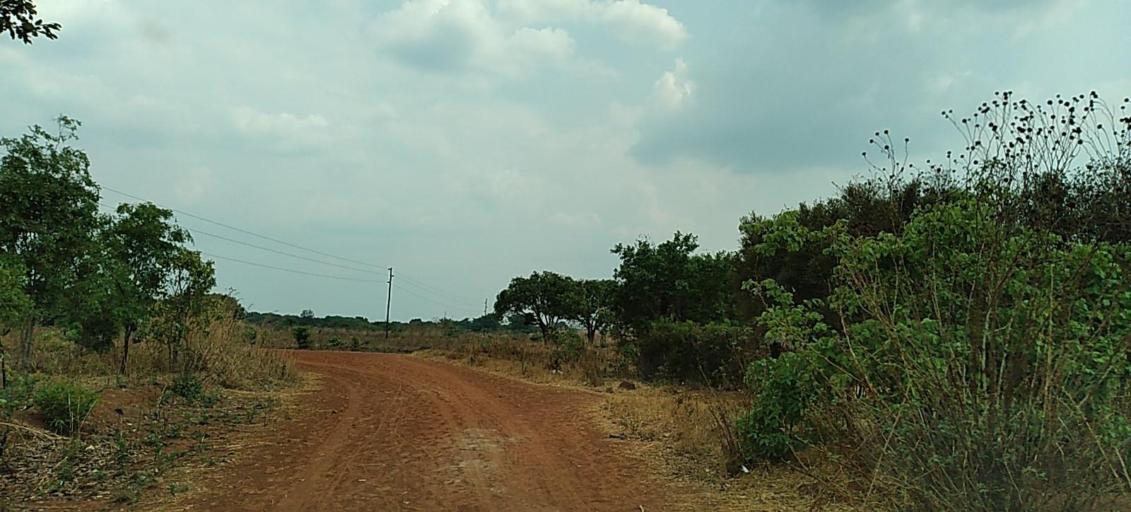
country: ZM
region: Copperbelt
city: Kalulushi
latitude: -12.8912
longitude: 28.0753
